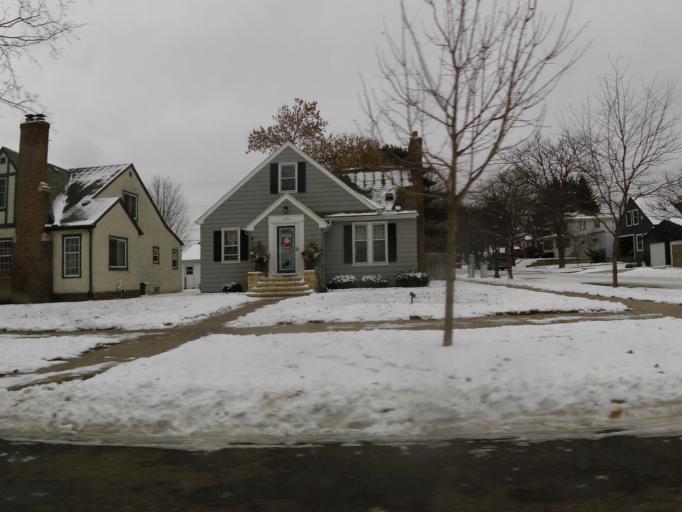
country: US
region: Minnesota
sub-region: Dakota County
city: Mendota Heights
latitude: 44.9288
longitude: -93.1501
